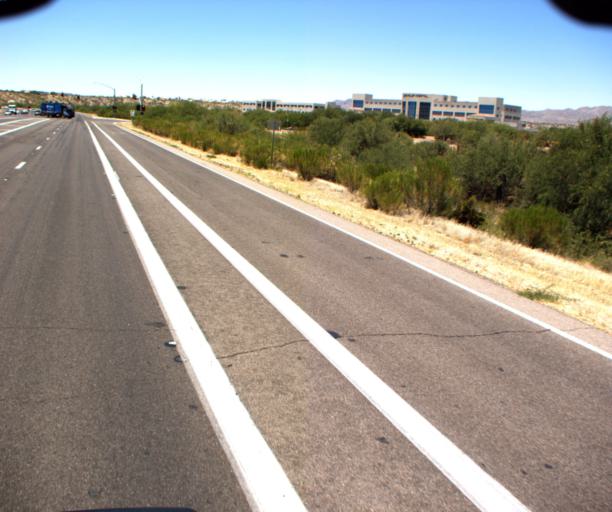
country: US
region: Arizona
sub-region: Pima County
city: Oro Valley
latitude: 32.4273
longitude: -110.9450
